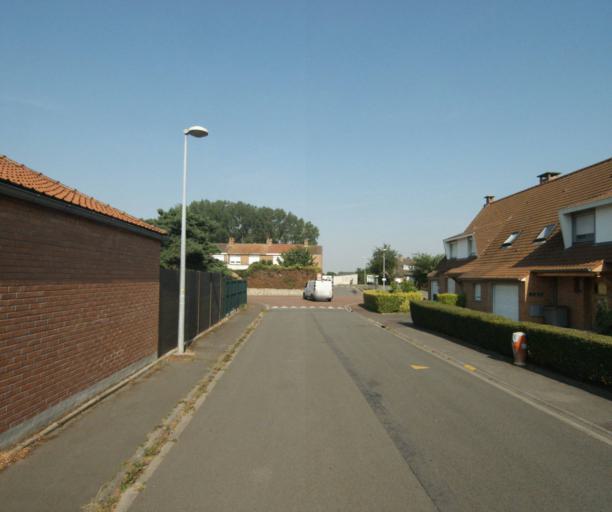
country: FR
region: Nord-Pas-de-Calais
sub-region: Departement du Nord
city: Quesnoy-sur-Deule
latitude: 50.7170
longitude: 2.9978
